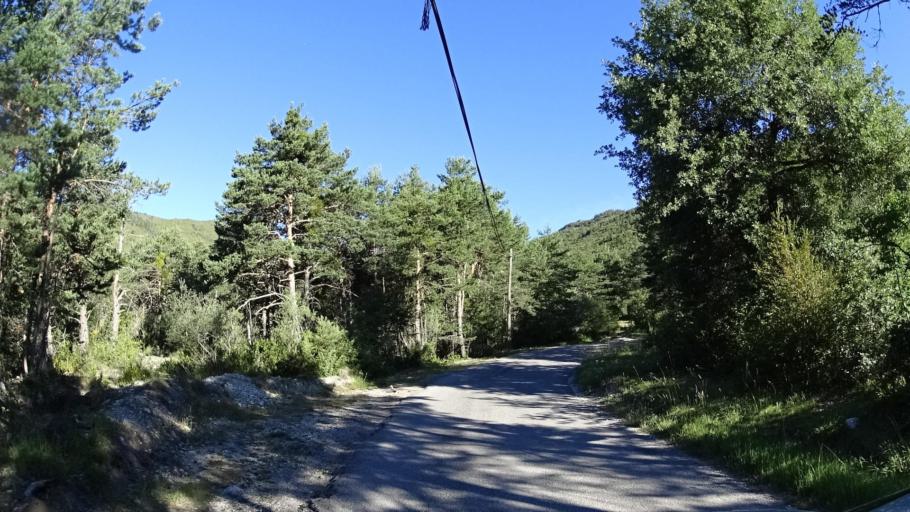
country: FR
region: Provence-Alpes-Cote d'Azur
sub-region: Departement des Alpes-de-Haute-Provence
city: Castellane
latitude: 43.8790
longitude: 6.5025
